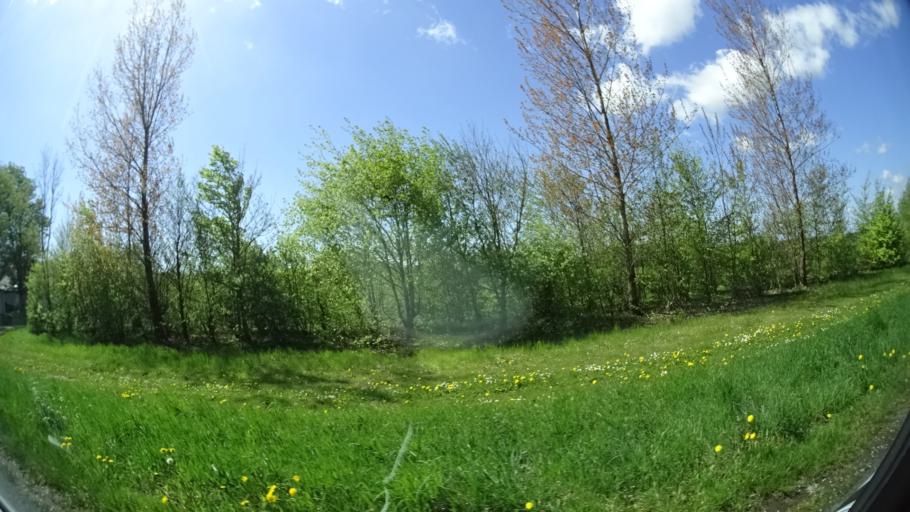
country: DK
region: Central Jutland
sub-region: Arhus Kommune
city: Framlev
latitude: 56.1209
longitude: 10.0170
